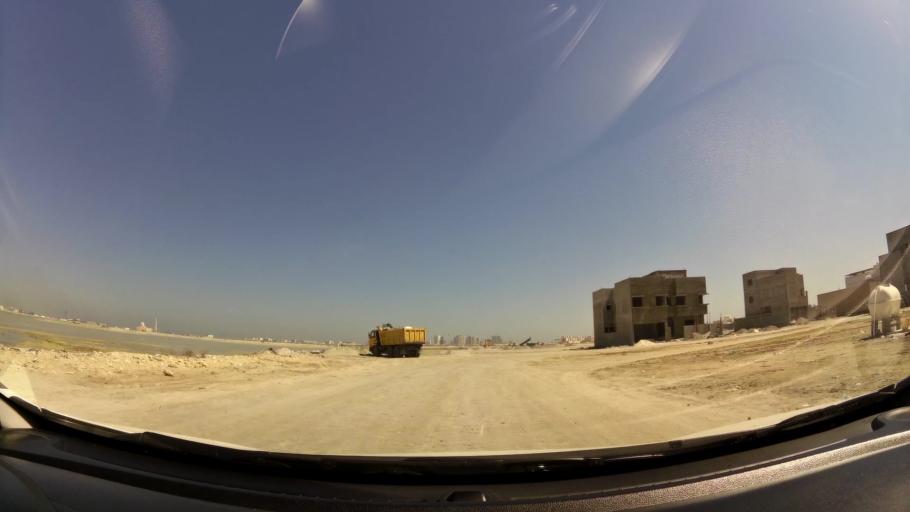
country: BH
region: Muharraq
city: Al Muharraq
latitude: 26.2882
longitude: 50.6312
